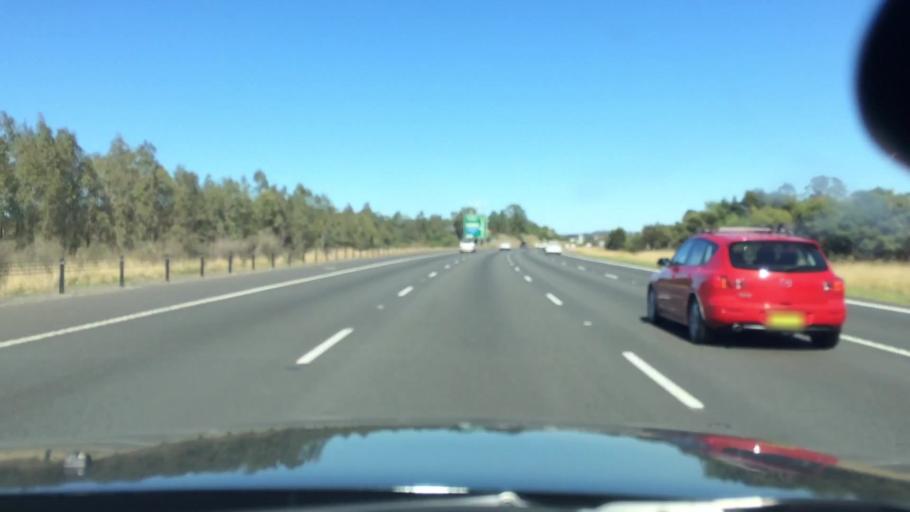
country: AU
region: New South Wales
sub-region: Campbelltown Municipality
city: Ingleburn
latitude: -33.9796
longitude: 150.8679
